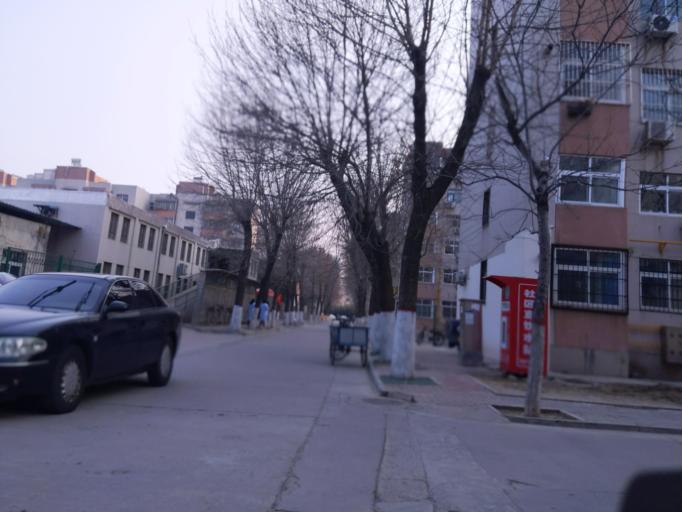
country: CN
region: Henan Sheng
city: Zhongyuanlu
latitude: 35.7812
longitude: 115.0537
